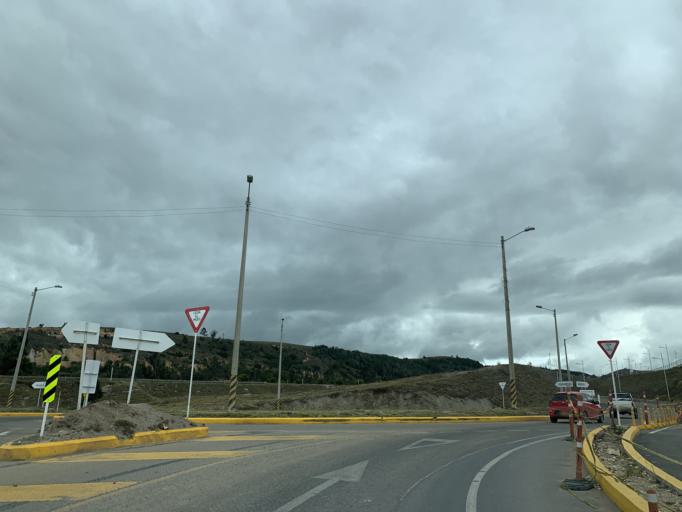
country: CO
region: Boyaca
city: Tunja
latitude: 5.5324
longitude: -73.3440
